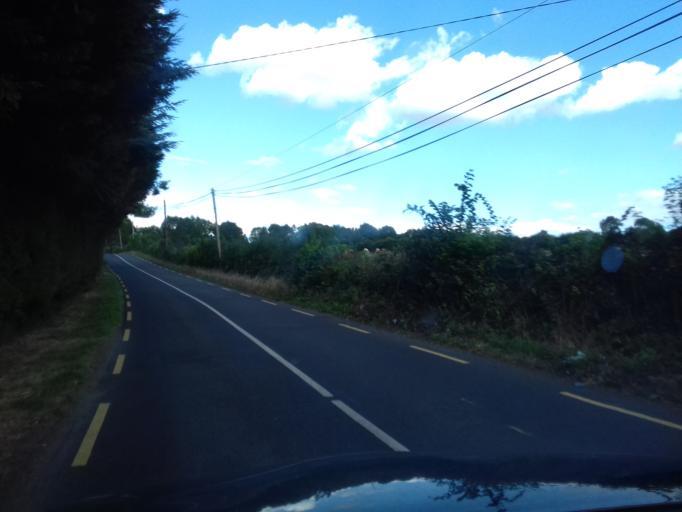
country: IE
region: Leinster
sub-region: Kilkenny
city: Thomastown
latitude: 52.5292
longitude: -7.1219
